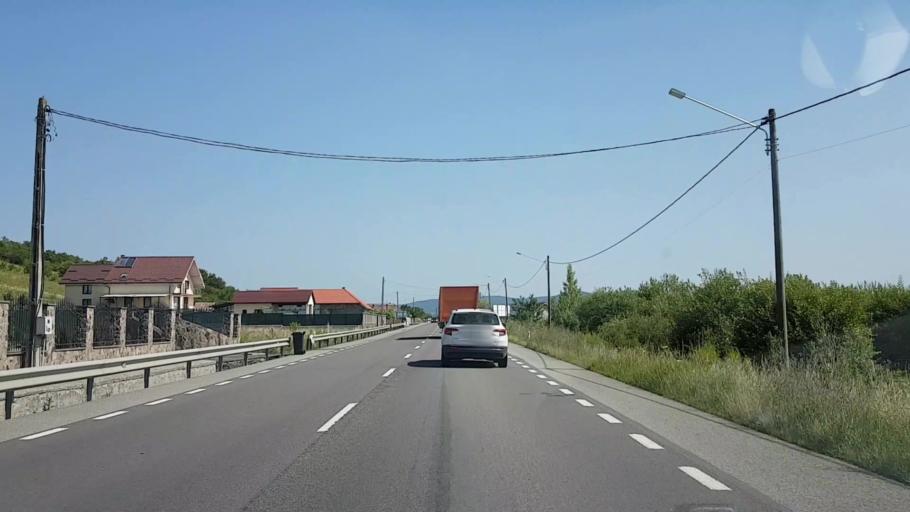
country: RO
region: Bistrita-Nasaud
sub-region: Comuna Sieu-Odorhei
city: Sieu-Odorhei
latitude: 47.1342
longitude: 24.3092
